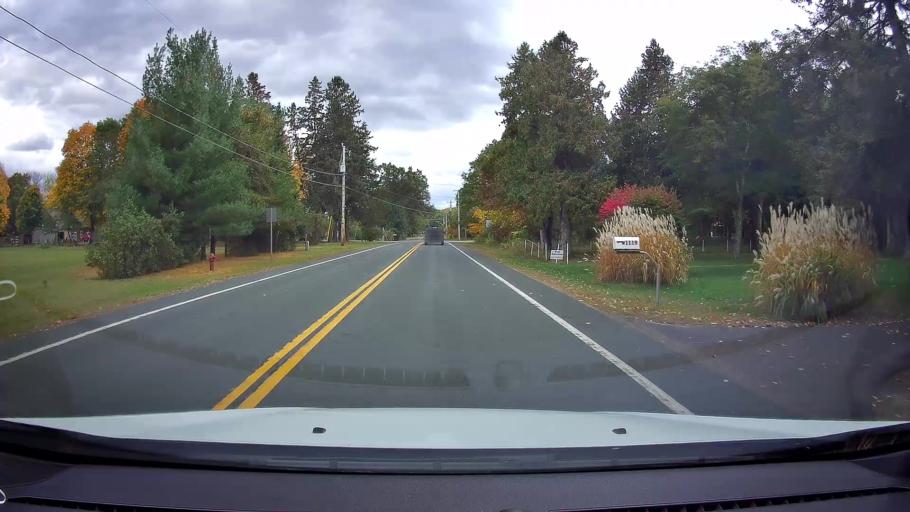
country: US
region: Wisconsin
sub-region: Polk County
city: Saint Croix Falls
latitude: 45.4156
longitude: -92.6621
